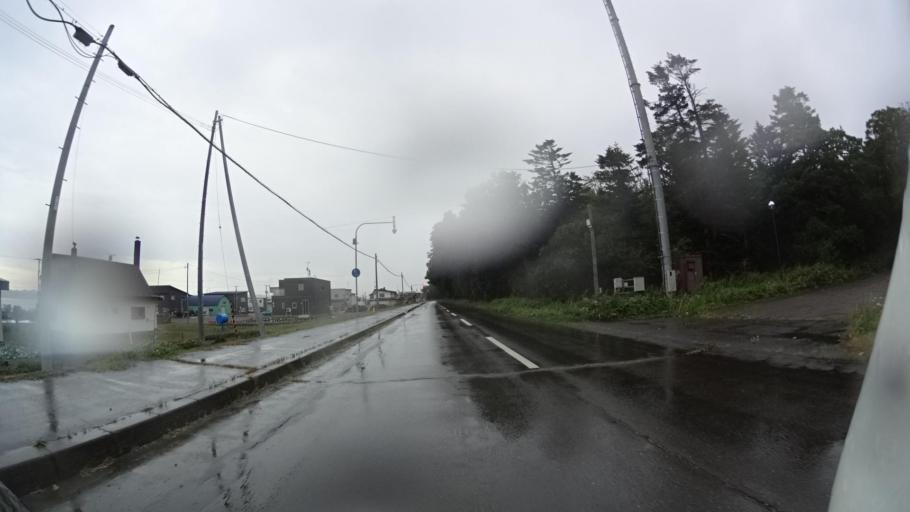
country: JP
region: Hokkaido
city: Kitami
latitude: 44.1883
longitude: 143.7511
